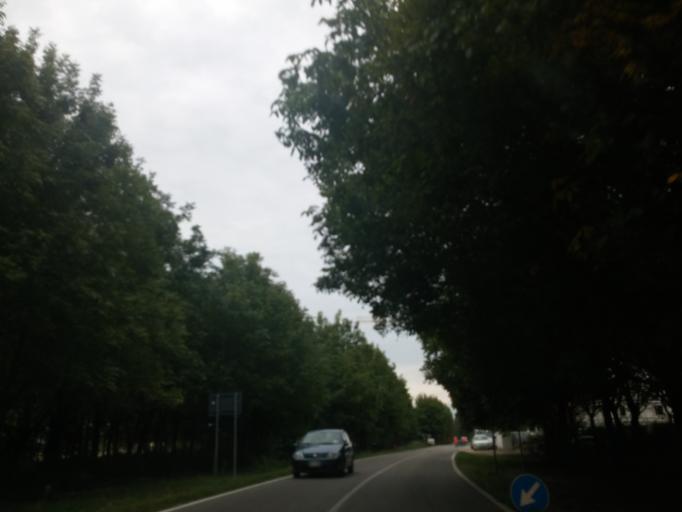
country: IT
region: Emilia-Romagna
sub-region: Provincia di Bologna
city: Trebbo
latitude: 44.5769
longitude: 11.3256
